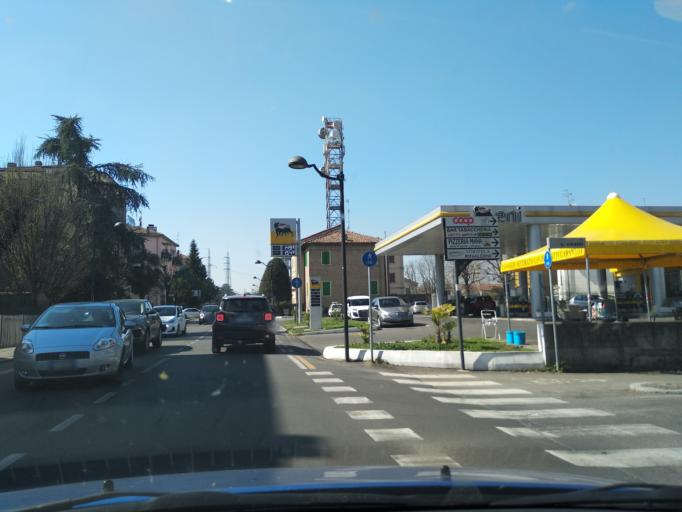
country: IT
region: Emilia-Romagna
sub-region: Provincia di Reggio Emilia
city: Reggio nell'Emilia
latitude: 44.6973
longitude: 10.6140
